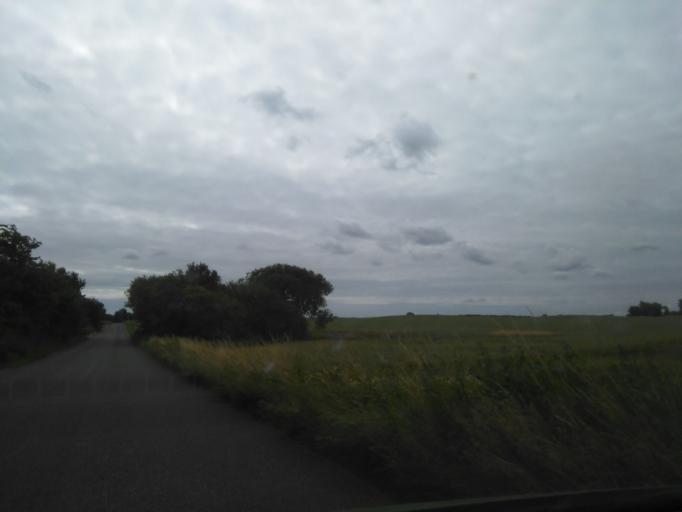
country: DK
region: Central Jutland
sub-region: Arhus Kommune
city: Solbjerg
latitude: 56.0255
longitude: 10.0691
